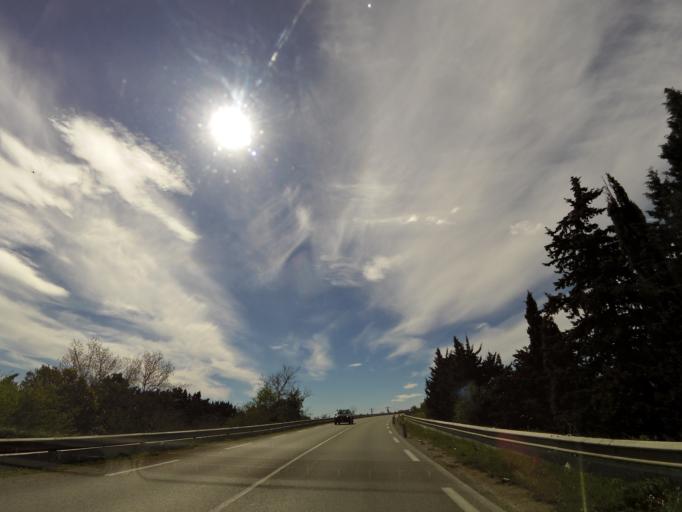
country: FR
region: Languedoc-Roussillon
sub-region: Departement de l'Herault
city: Lunel
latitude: 43.6793
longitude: 4.1510
